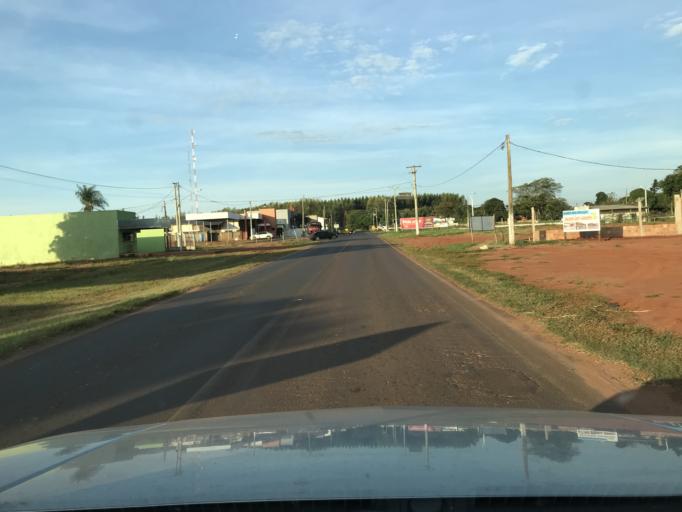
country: BR
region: Mato Grosso do Sul
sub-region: Iguatemi
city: Iguatemi
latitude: -23.6627
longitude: -54.5645
